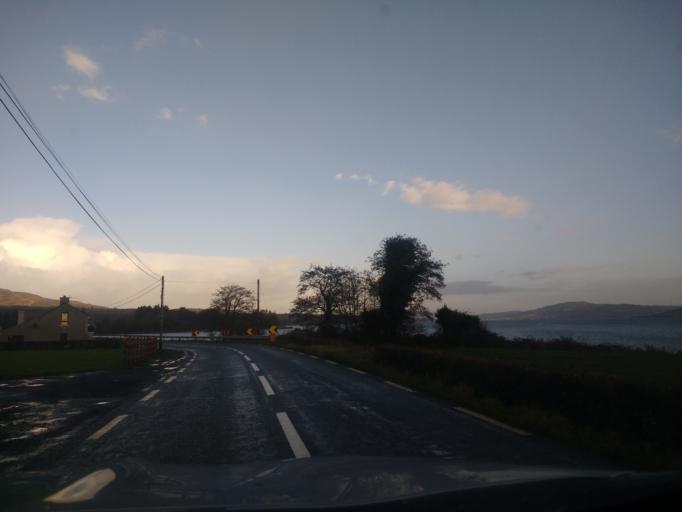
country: IE
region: Ulster
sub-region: County Donegal
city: Ramelton
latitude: 55.0693
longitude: -7.5996
